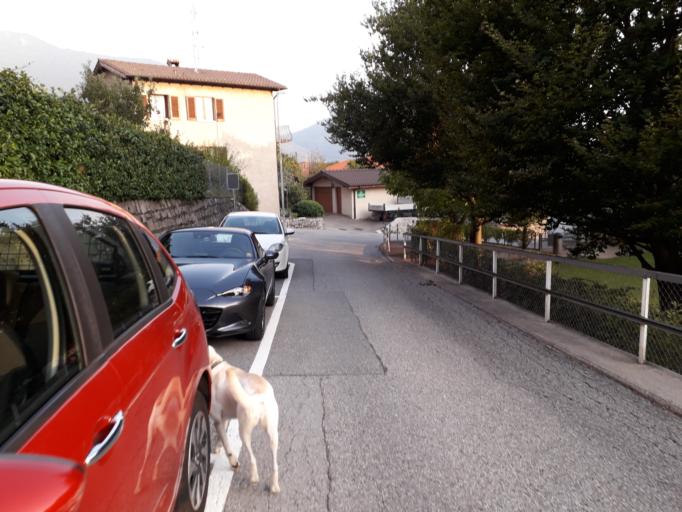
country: CH
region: Ticino
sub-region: Lugano District
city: Comano
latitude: 46.0382
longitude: 8.9543
